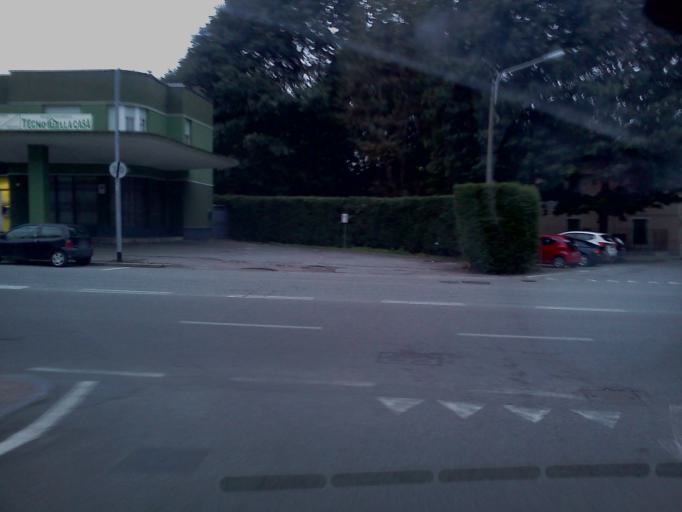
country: IT
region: Piedmont
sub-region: Provincia di Biella
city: Biella
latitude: 45.5583
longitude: 8.0409
